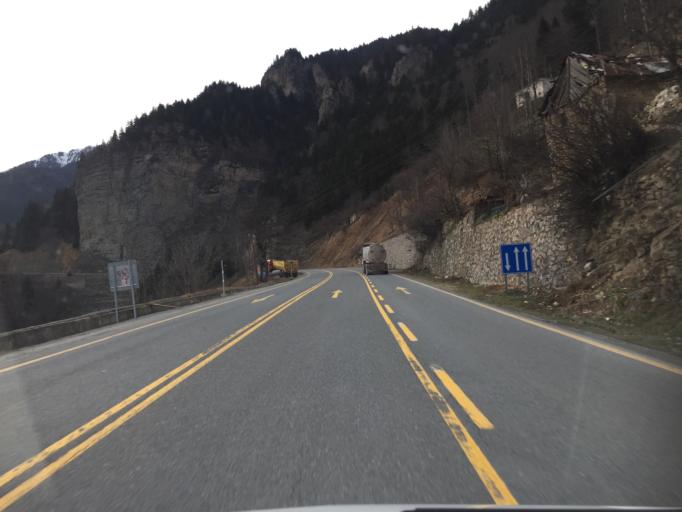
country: TR
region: Gumushane
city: Yaglidere
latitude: 40.6990
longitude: 39.4831
